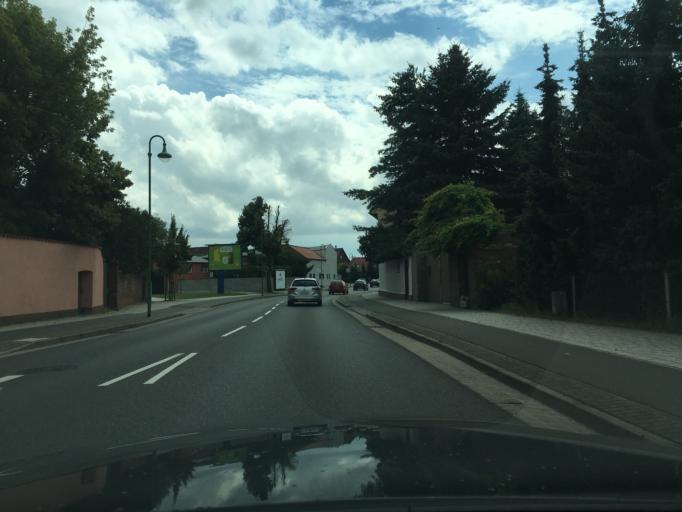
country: DE
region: Saxony-Anhalt
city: Bobbau
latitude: 51.6909
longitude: 12.2647
